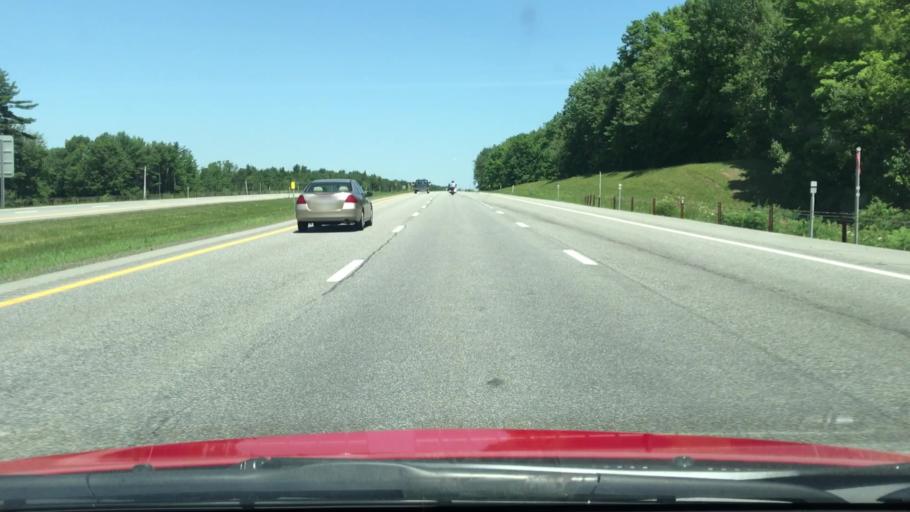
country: US
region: New York
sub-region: Essex County
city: Keeseville
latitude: 44.4483
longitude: -73.4894
